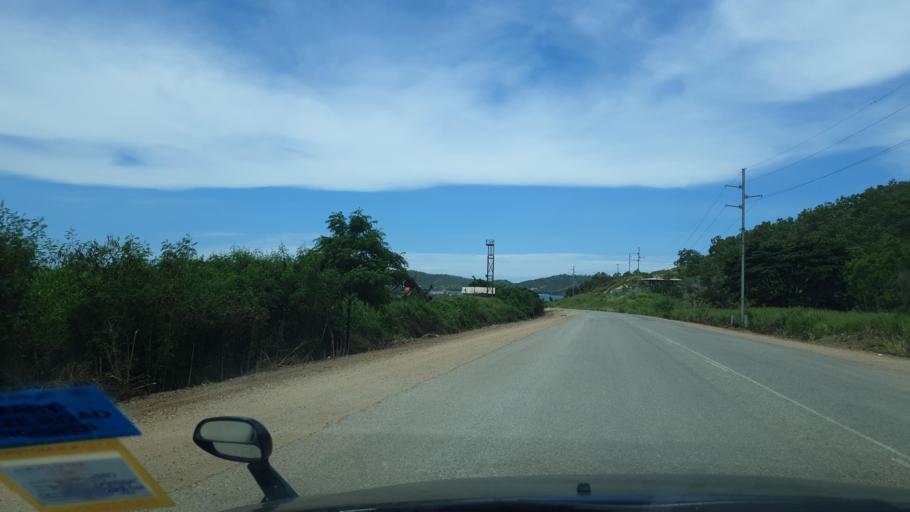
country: PG
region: National Capital
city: Port Moresby
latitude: -9.4160
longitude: 147.1001
